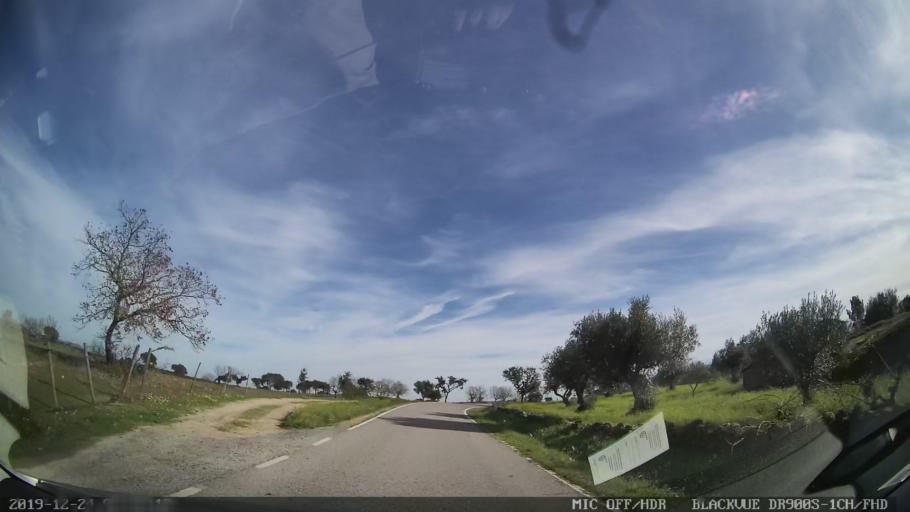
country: PT
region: Portalegre
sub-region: Nisa
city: Nisa
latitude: 39.4874
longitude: -7.7367
